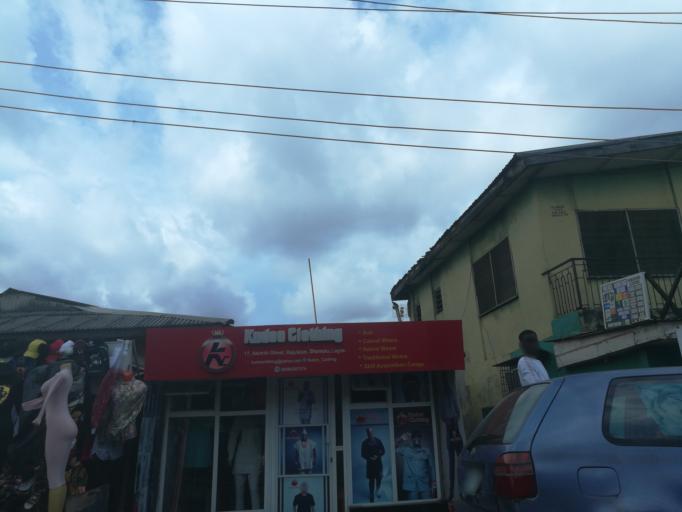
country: NG
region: Lagos
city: Somolu
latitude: 6.5309
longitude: 3.3836
